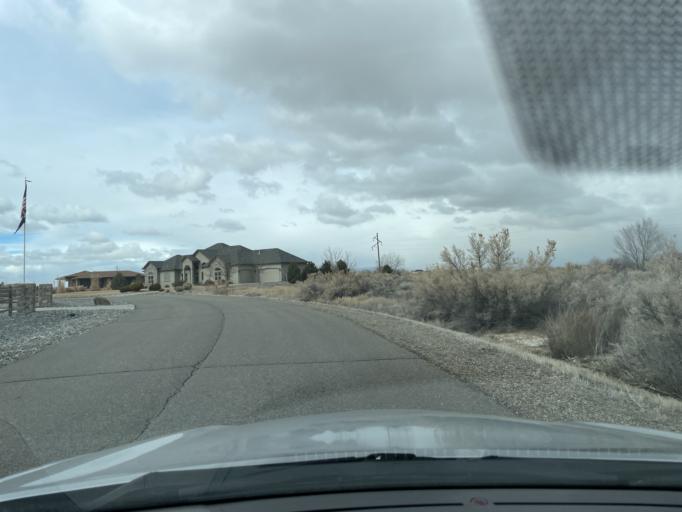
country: US
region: Colorado
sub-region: Mesa County
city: Loma
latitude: 39.2178
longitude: -108.8046
